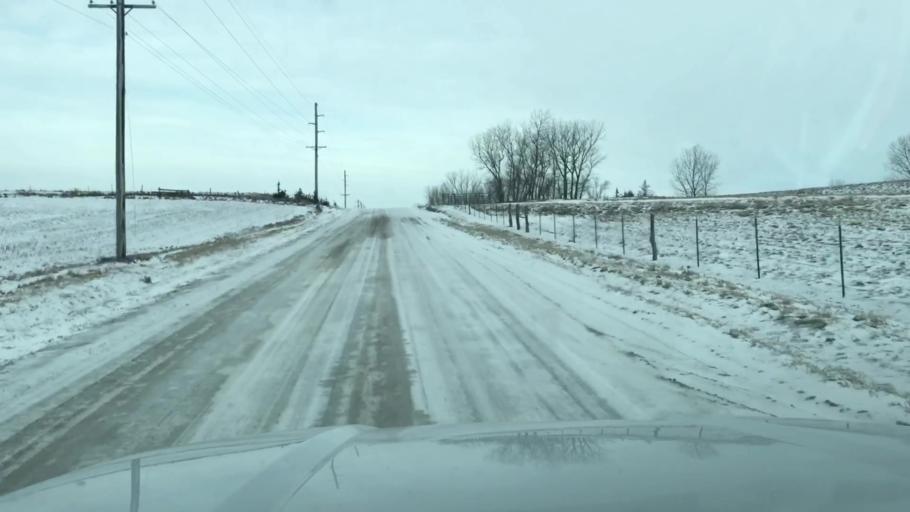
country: US
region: Missouri
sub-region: Holt County
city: Oregon
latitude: 40.1301
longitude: -95.0597
